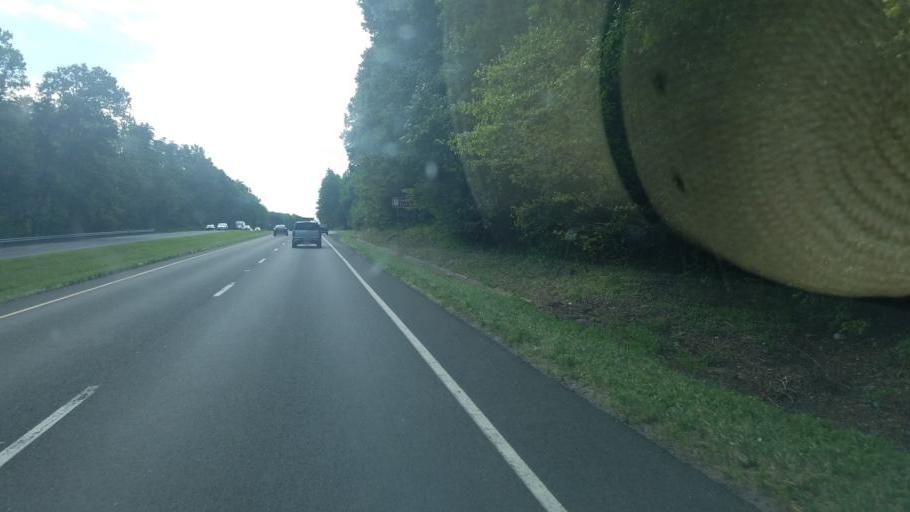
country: US
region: Virginia
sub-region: Fauquier County
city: Bealeton
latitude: 38.4576
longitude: -77.6644
